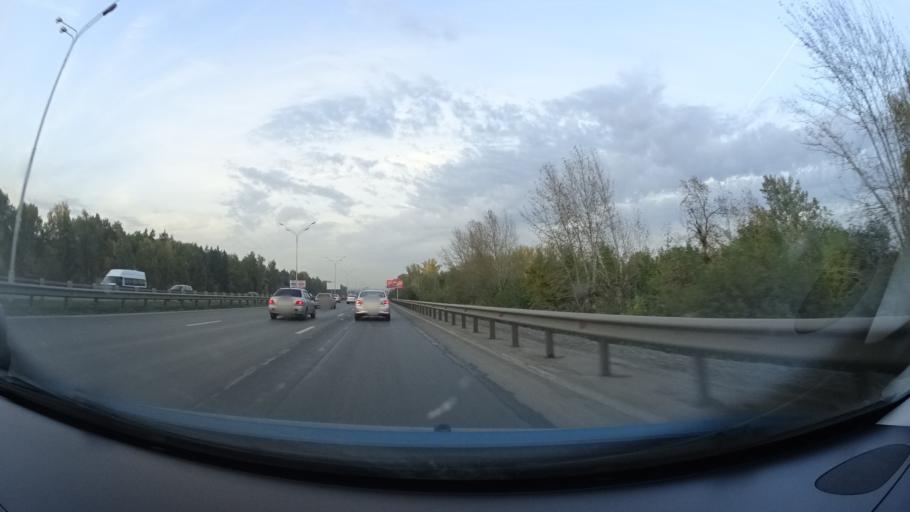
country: RU
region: Bashkortostan
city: Ufa
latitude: 54.6858
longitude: 55.9379
